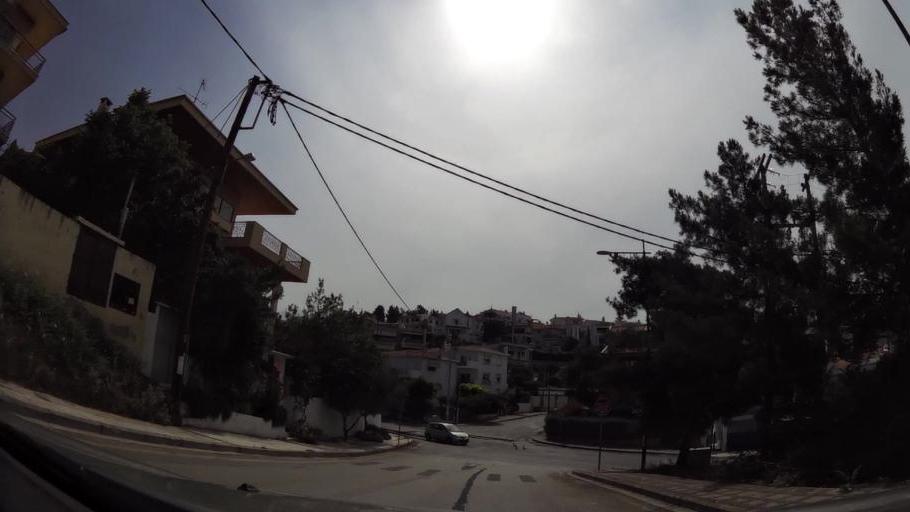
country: GR
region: Central Macedonia
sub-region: Nomos Thessalonikis
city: Panorama
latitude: 40.5813
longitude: 23.0192
